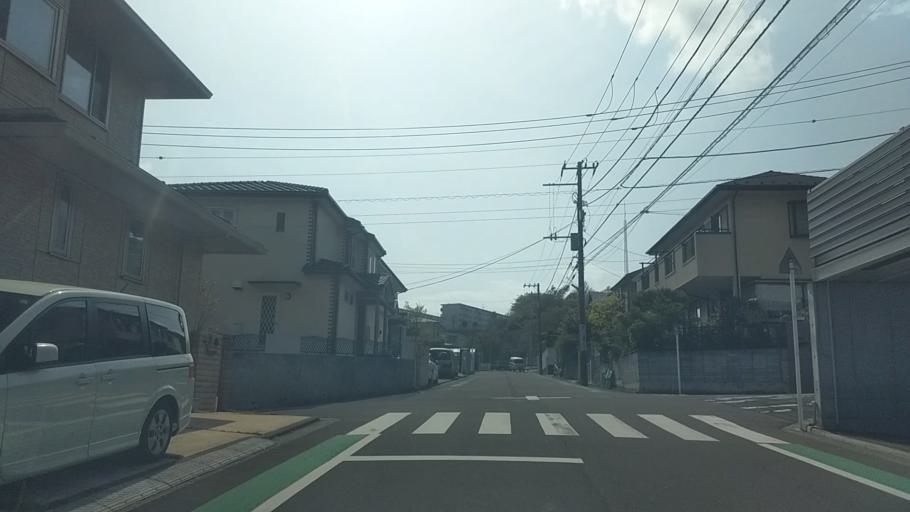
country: JP
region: Kanagawa
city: Kamakura
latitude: 35.3843
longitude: 139.5744
